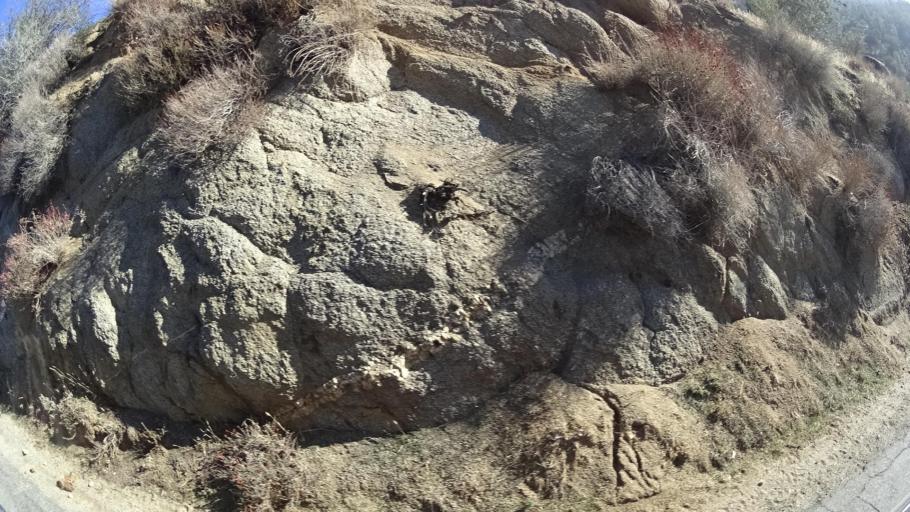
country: US
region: California
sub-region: Kern County
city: Bodfish
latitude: 35.5562
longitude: -118.5801
